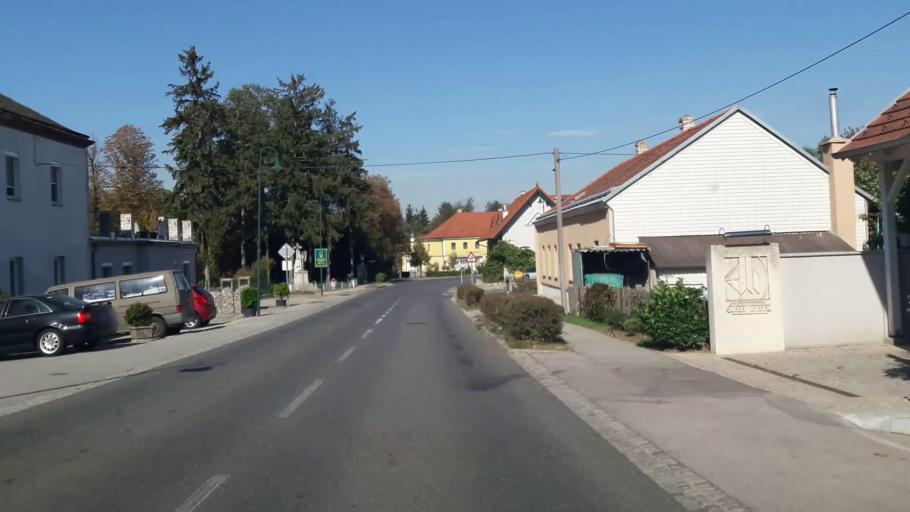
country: AT
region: Lower Austria
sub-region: Politischer Bezirk Korneuburg
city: Grossrussbach
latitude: 48.4592
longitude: 16.3731
